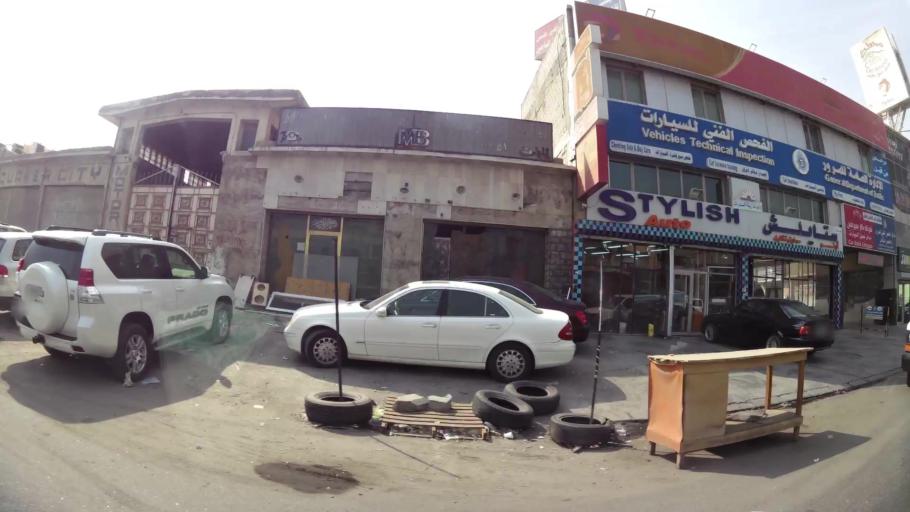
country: KW
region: Al Asimah
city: Ar Rabiyah
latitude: 29.3175
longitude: 47.9330
